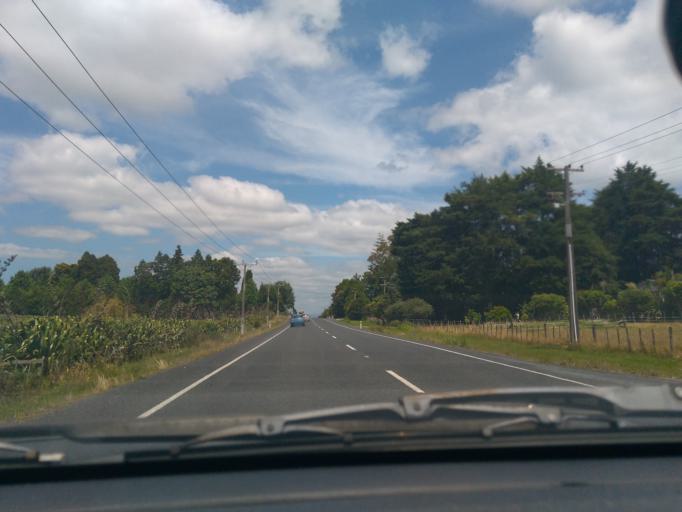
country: NZ
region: Northland
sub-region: Far North District
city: Kerikeri
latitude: -35.1751
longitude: 173.9015
